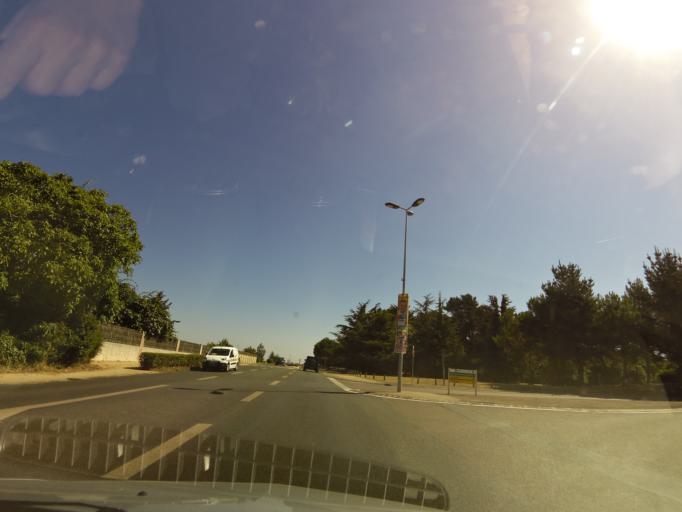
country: FR
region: Pays de la Loire
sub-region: Departement de la Vendee
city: Jard-sur-Mer
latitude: 46.4154
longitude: -1.5414
